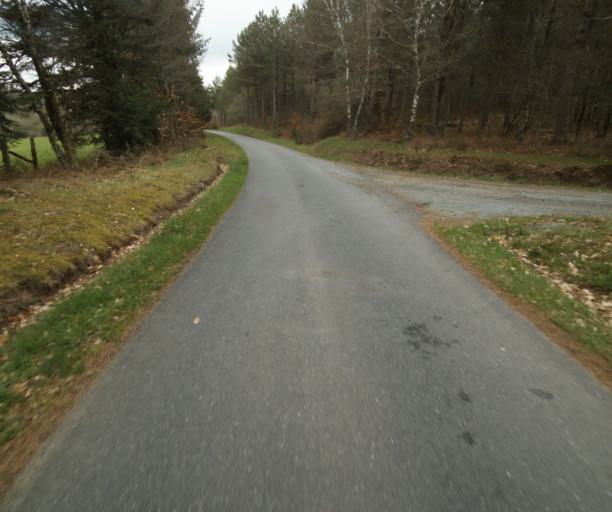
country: FR
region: Limousin
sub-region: Departement de la Correze
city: Correze
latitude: 45.3067
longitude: 1.9057
